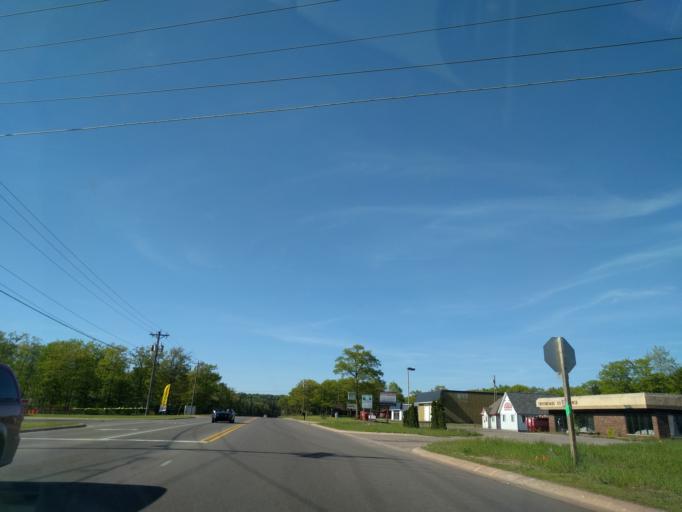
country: US
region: Michigan
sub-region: Marquette County
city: Harvey
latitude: 46.4643
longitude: -87.4254
